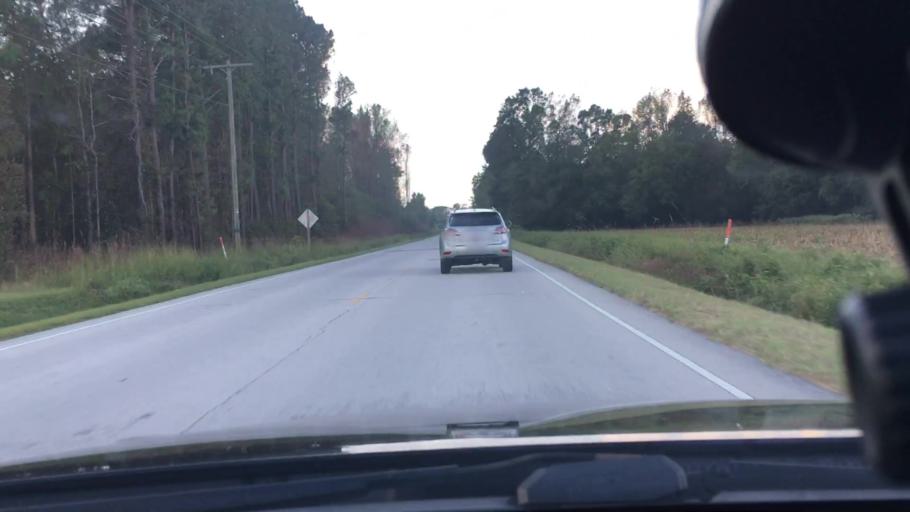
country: US
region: North Carolina
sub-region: Craven County
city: Vanceboro
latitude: 35.3673
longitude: -77.2037
